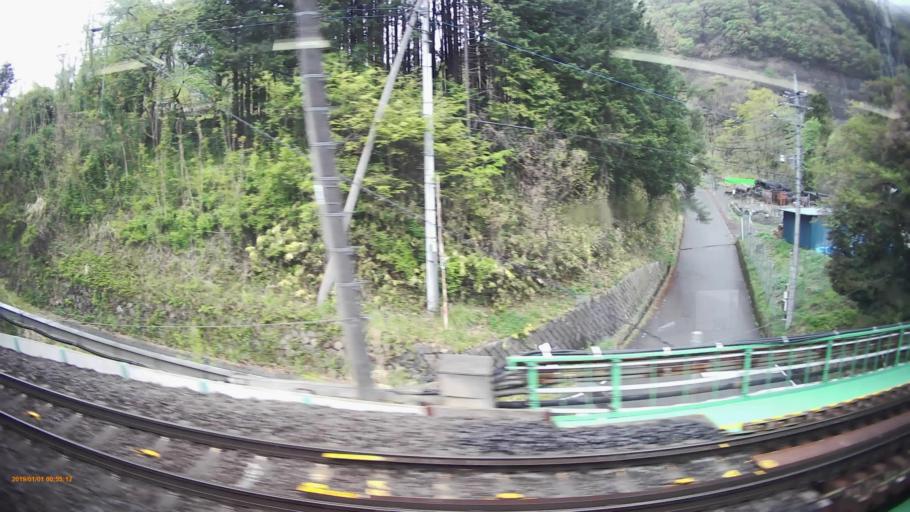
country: JP
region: Yamanashi
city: Otsuki
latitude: 35.6023
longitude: 138.8498
